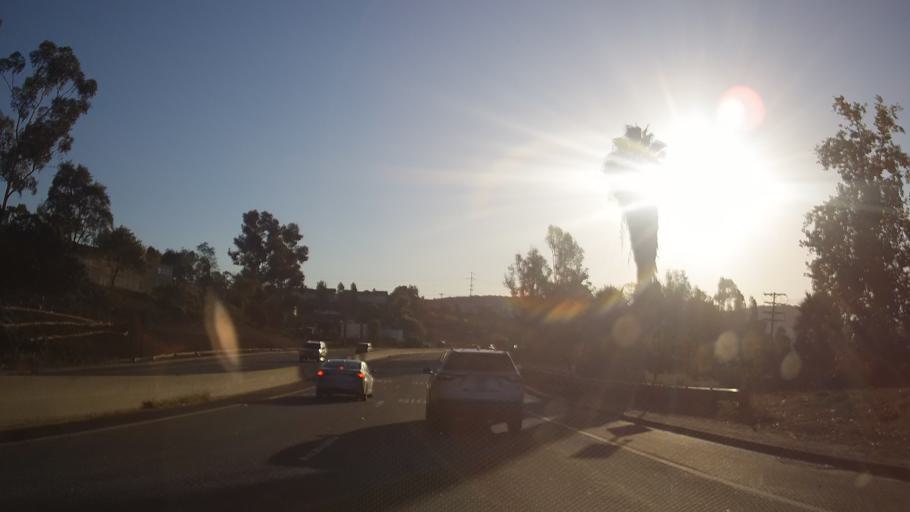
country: US
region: California
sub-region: San Diego County
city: Casa de Oro-Mount Helix
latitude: 32.7456
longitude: -116.9604
